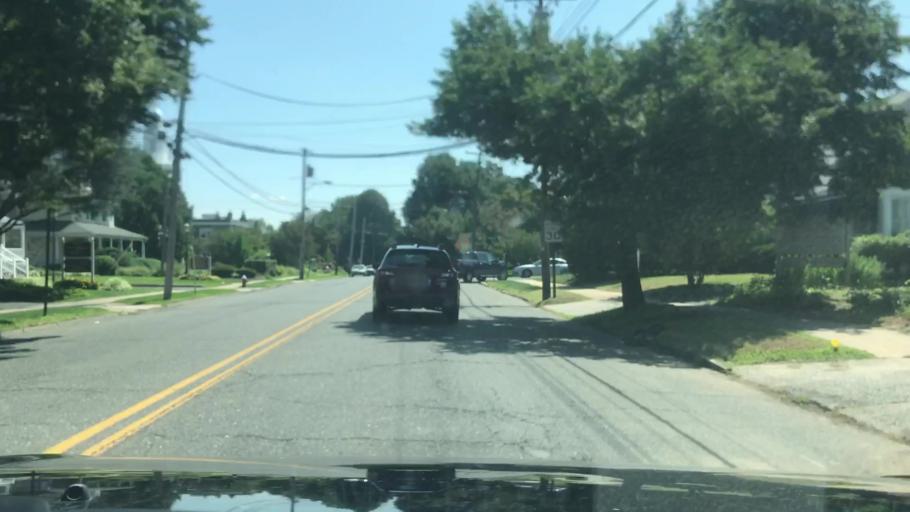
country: US
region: New Jersey
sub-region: Monmouth County
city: Red Bank
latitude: 40.3449
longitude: -74.0647
